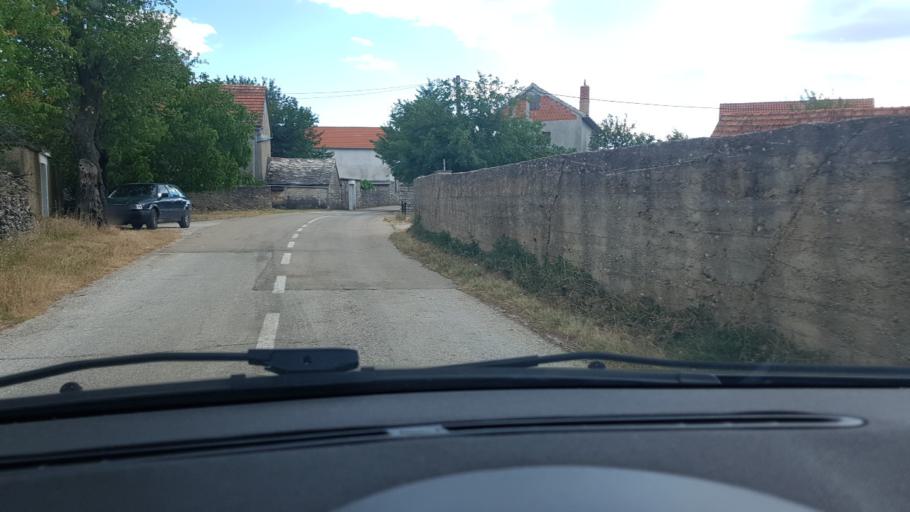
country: HR
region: Sibensko-Kniniska
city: Kistanje
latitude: 44.0560
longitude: 15.9253
